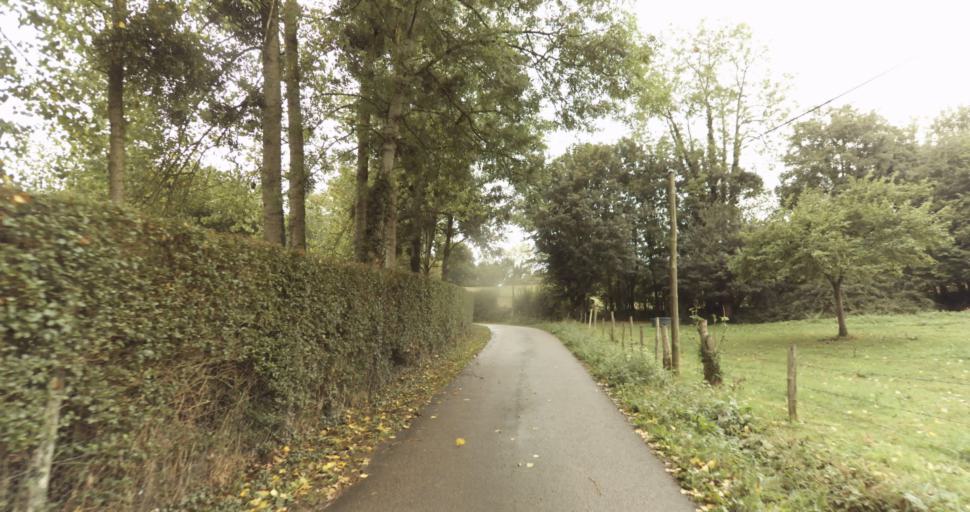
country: FR
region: Lower Normandy
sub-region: Departement de l'Orne
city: Vimoutiers
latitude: 48.8906
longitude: 0.2094
